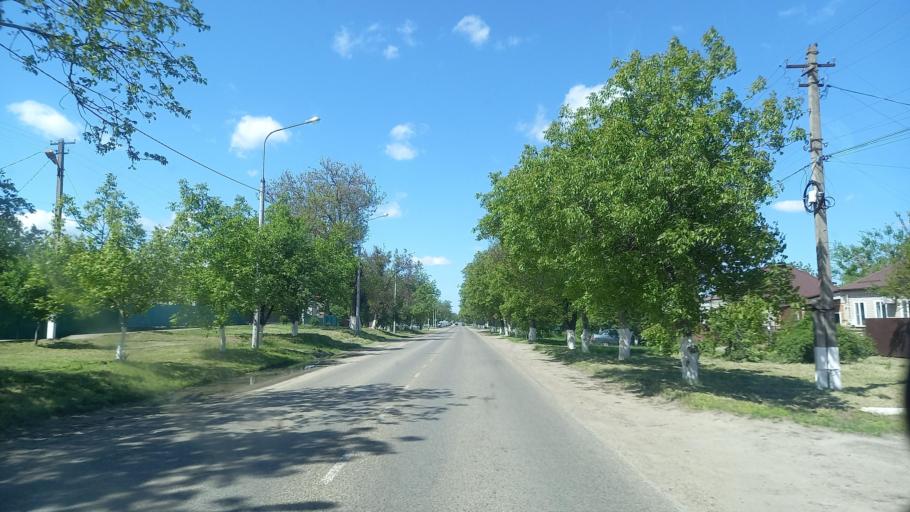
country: RU
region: Krasnodarskiy
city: Novoukrainskoye
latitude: 45.3804
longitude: 40.5190
